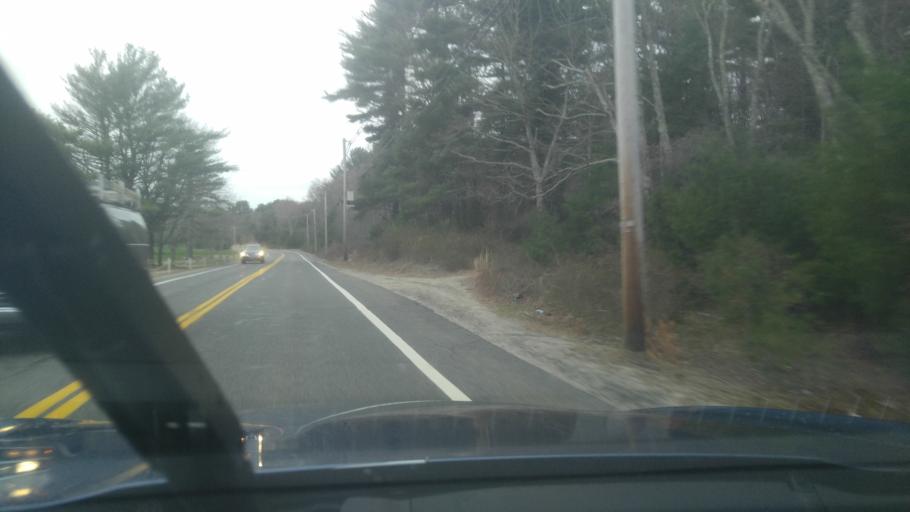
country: US
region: Rhode Island
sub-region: Kent County
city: West Greenwich
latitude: 41.6703
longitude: -71.6278
